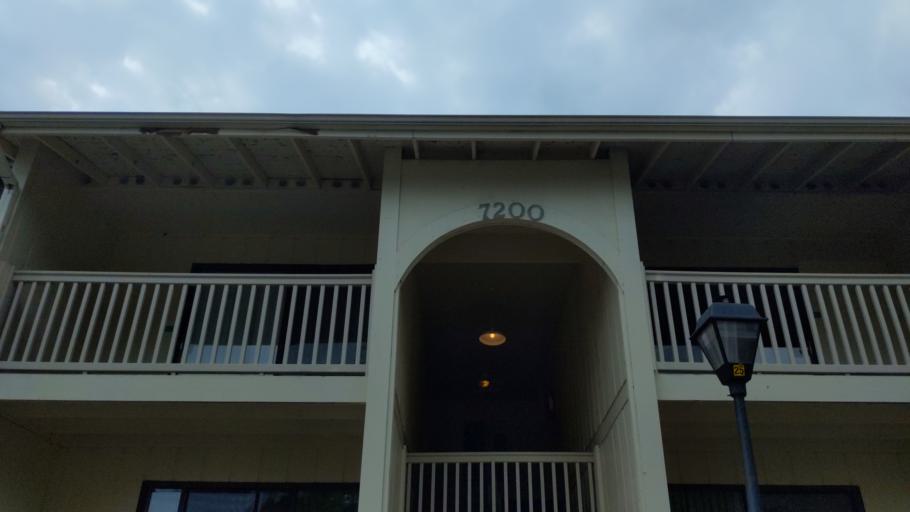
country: US
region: Virginia
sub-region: Montgomery County
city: Blacksburg
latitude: 37.2432
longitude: -80.4231
